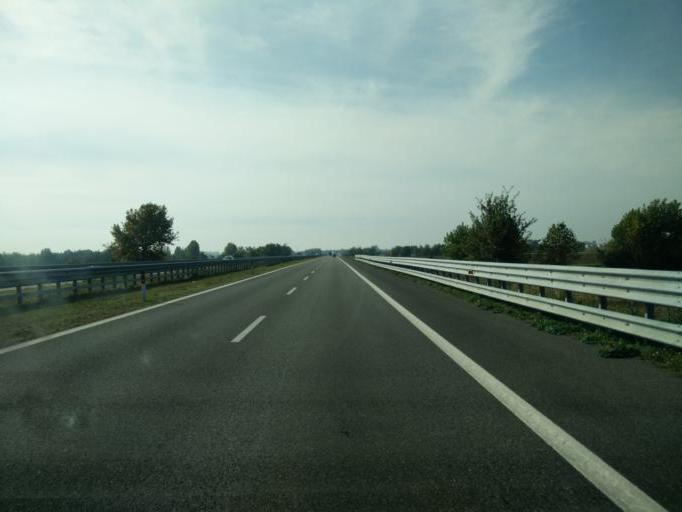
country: IT
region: Lombardy
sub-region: Provincia di Cremona
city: Corte de' Frati
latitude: 45.2309
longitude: 10.1159
